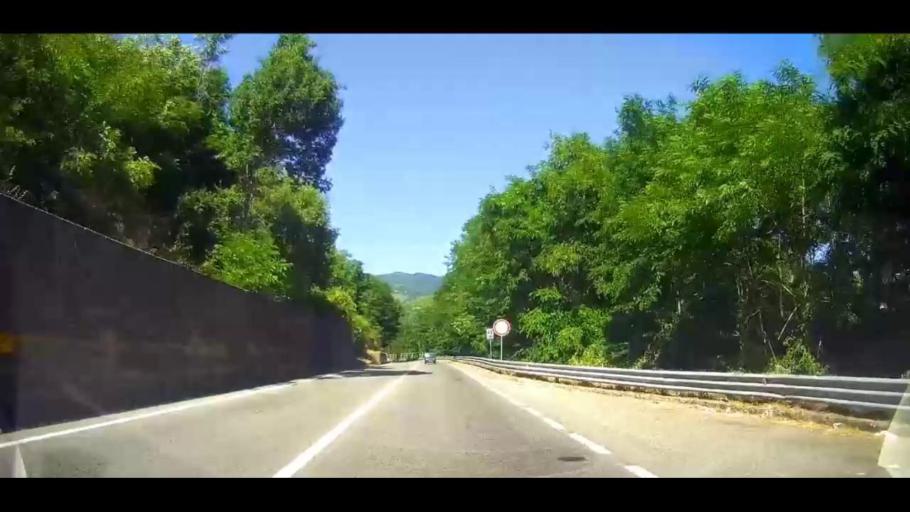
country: IT
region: Calabria
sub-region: Provincia di Cosenza
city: Rovito
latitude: 39.3109
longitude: 16.3275
